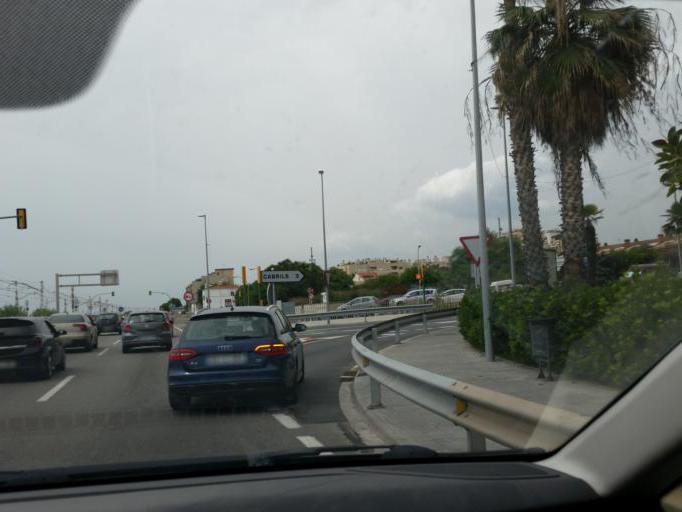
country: ES
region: Catalonia
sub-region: Provincia de Barcelona
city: Vilassar de Mar
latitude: 41.4986
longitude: 2.3852
